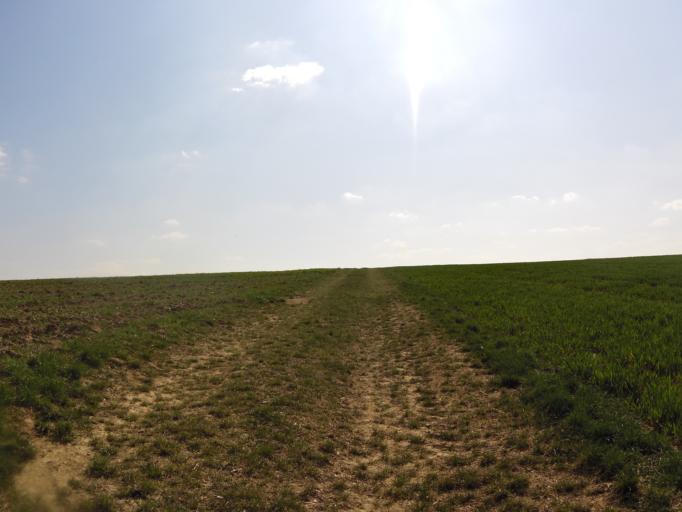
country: DE
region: Bavaria
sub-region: Regierungsbezirk Unterfranken
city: Dettelbach
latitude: 49.8173
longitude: 10.1444
